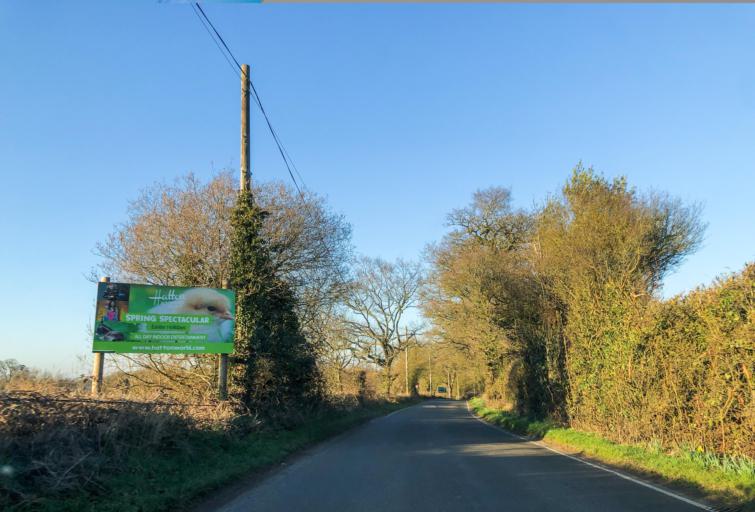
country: GB
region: England
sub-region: Warwickshire
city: Wroxall
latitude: 52.2952
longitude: -1.6589
